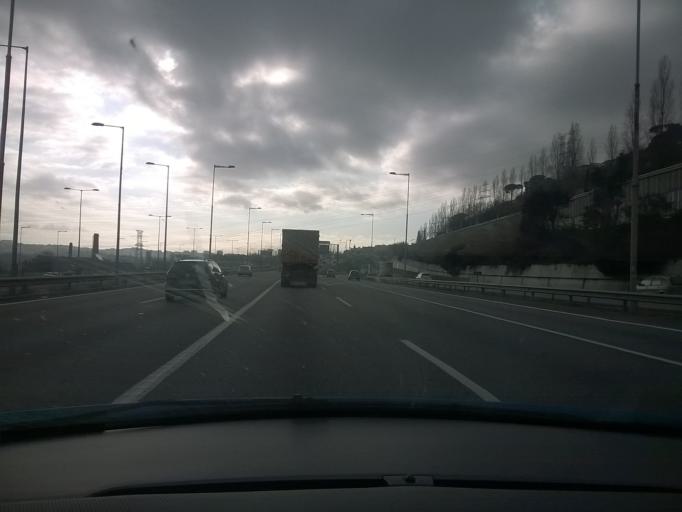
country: ES
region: Catalonia
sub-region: Provincia de Barcelona
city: Nou Barris
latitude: 41.4585
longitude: 2.1848
